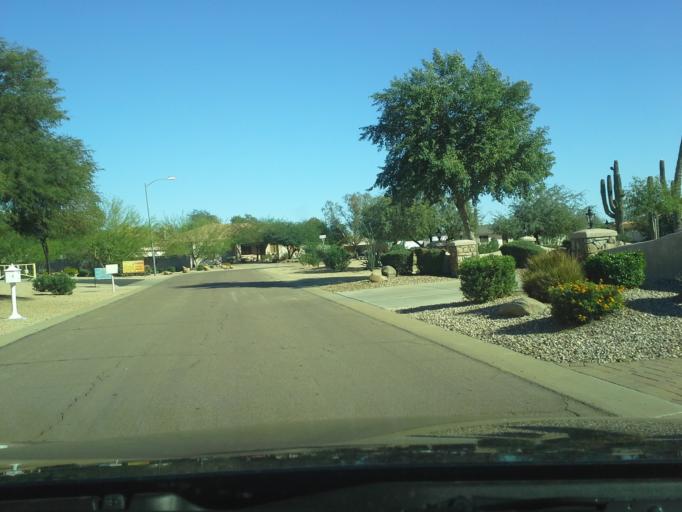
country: US
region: Arizona
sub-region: Maricopa County
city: Paradise Valley
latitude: 33.6389
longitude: -111.9928
